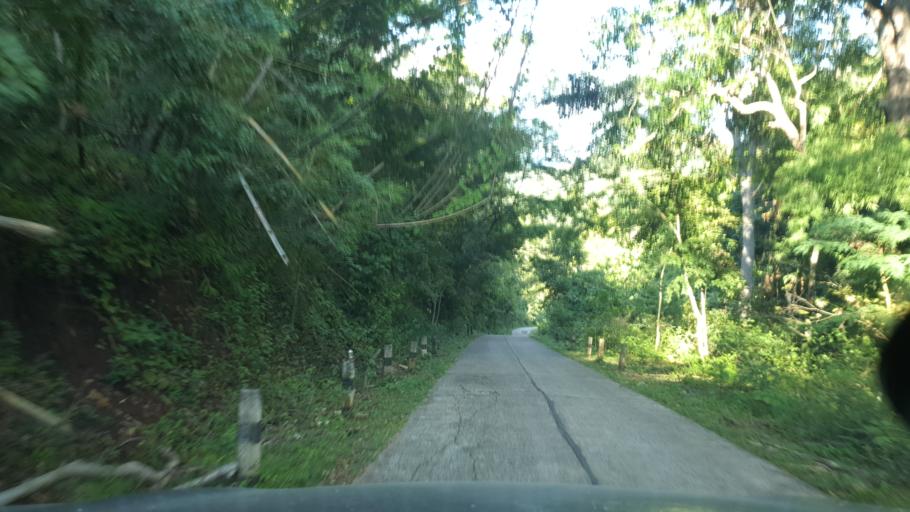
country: TH
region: Chiang Mai
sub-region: Amphoe Chiang Dao
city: Chiang Dao
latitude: 19.3931
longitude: 98.7703
